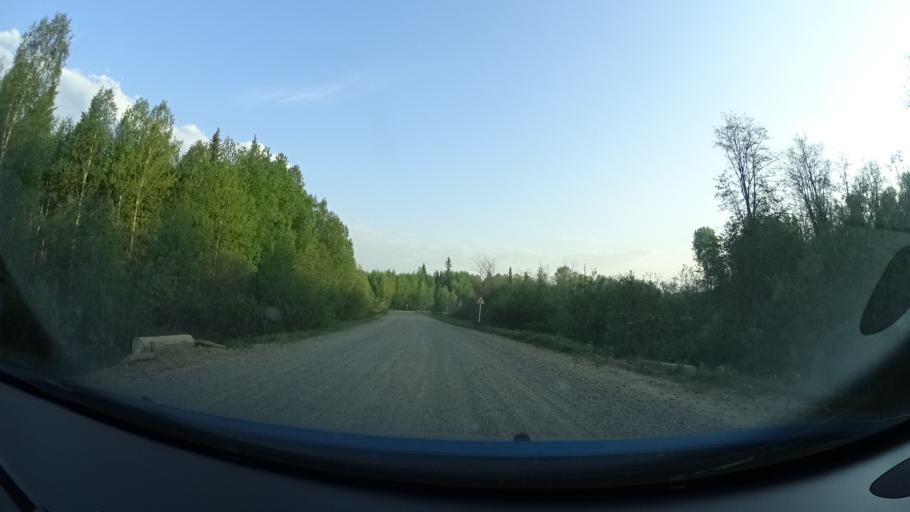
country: RU
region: Perm
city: Kuyeda
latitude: 56.6223
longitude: 55.7094
